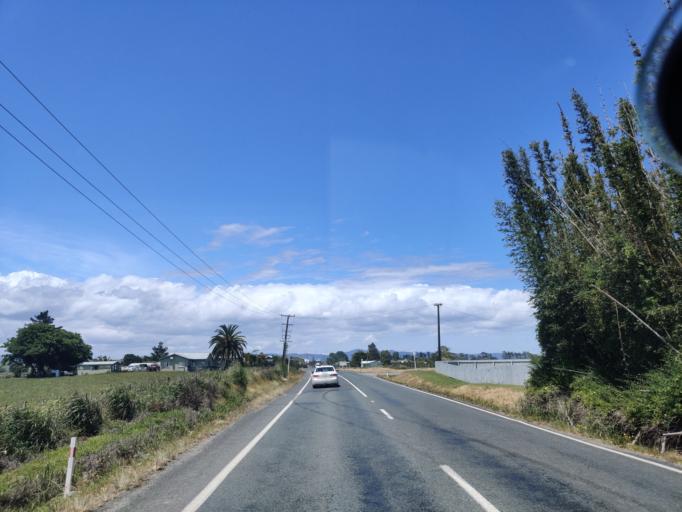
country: NZ
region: Northland
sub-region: Far North District
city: Kaitaia
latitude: -35.0338
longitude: 173.2542
